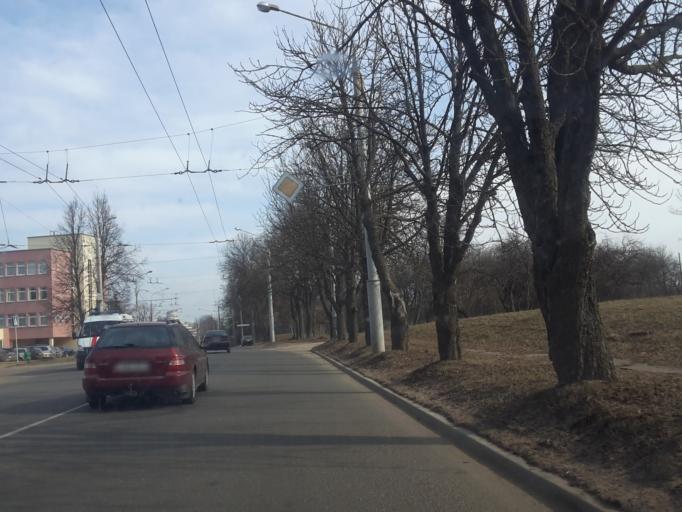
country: BY
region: Minsk
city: Minsk
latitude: 53.9011
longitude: 27.5178
